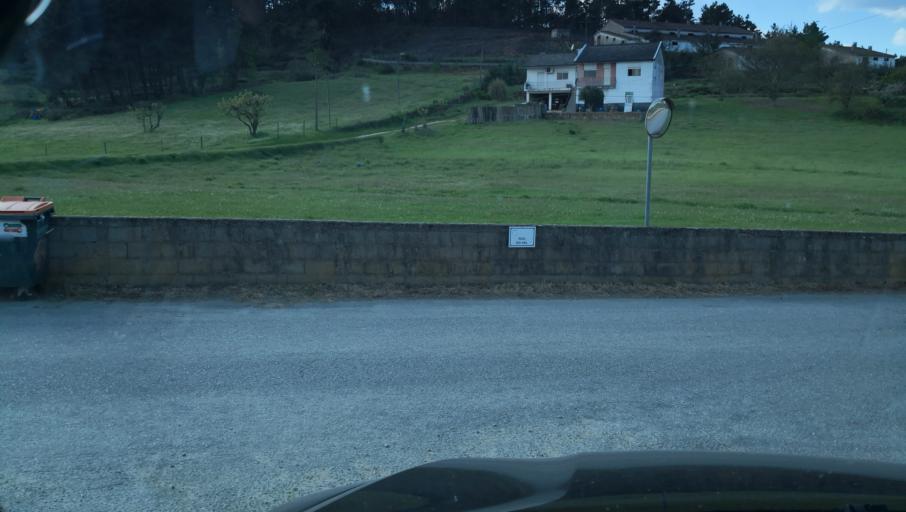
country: PT
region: Vila Real
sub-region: Sabrosa
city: Vilela
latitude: 41.2426
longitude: -7.6523
